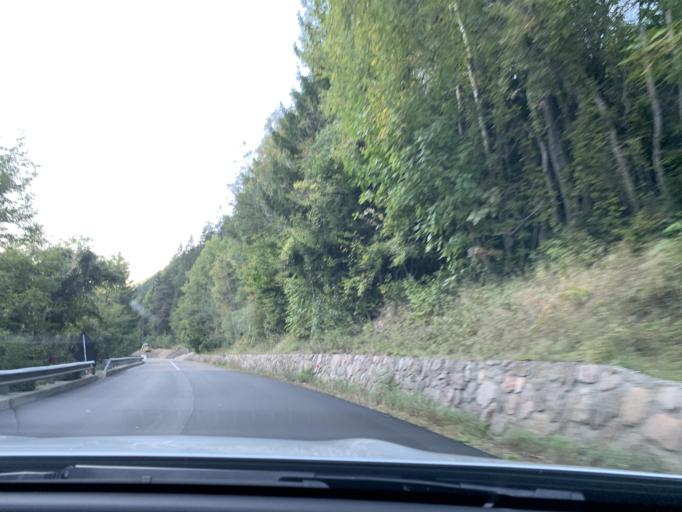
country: IT
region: Trentino-Alto Adige
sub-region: Bolzano
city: Nova Ponente
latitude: 46.4423
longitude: 11.4643
